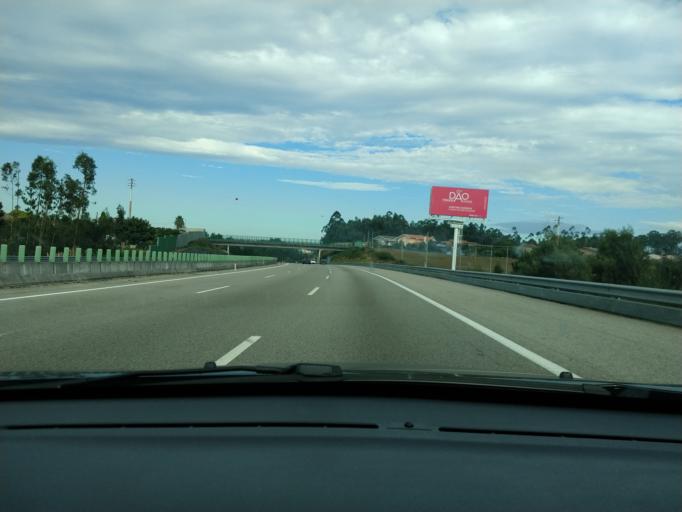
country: PT
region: Aveiro
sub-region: Santa Maria da Feira
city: Feira
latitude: 40.8833
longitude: -8.5624
